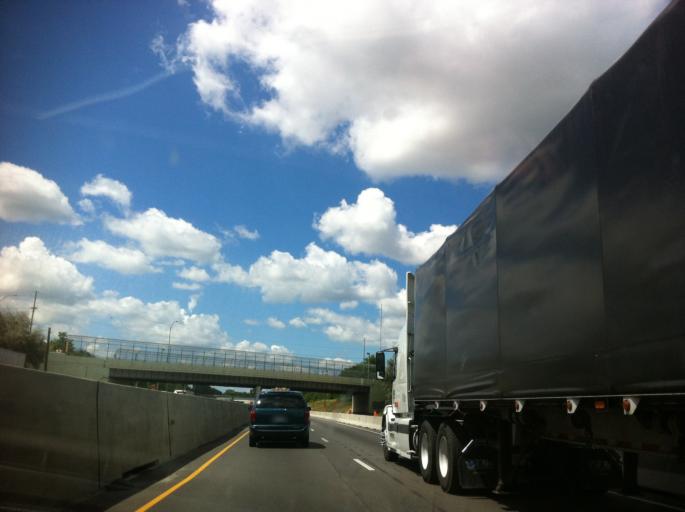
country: US
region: Ohio
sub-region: Lucas County
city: Toledo
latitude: 41.6543
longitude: -83.5535
